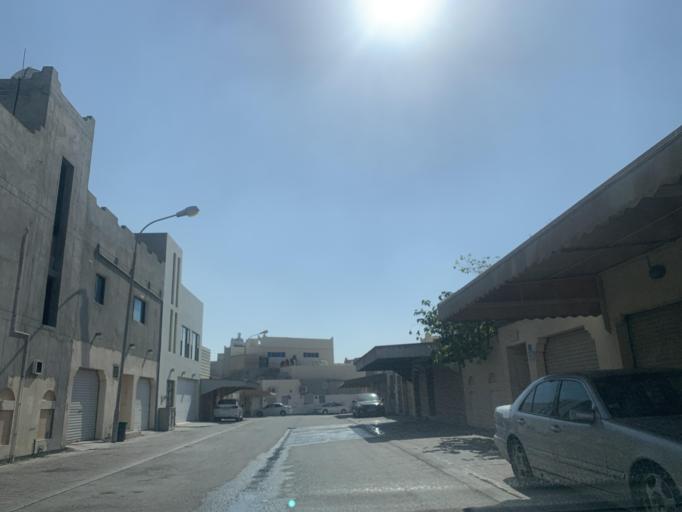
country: BH
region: Central Governorate
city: Madinat Hamad
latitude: 26.1225
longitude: 50.4959
